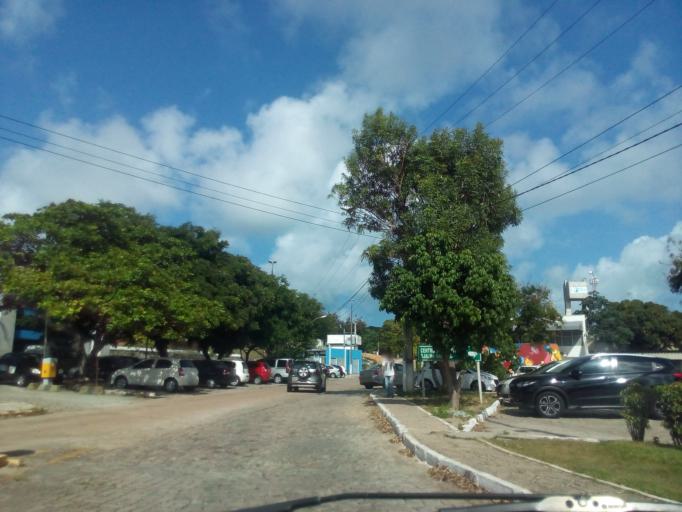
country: BR
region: Rio Grande do Norte
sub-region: Natal
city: Natal
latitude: -5.8385
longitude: -35.2008
